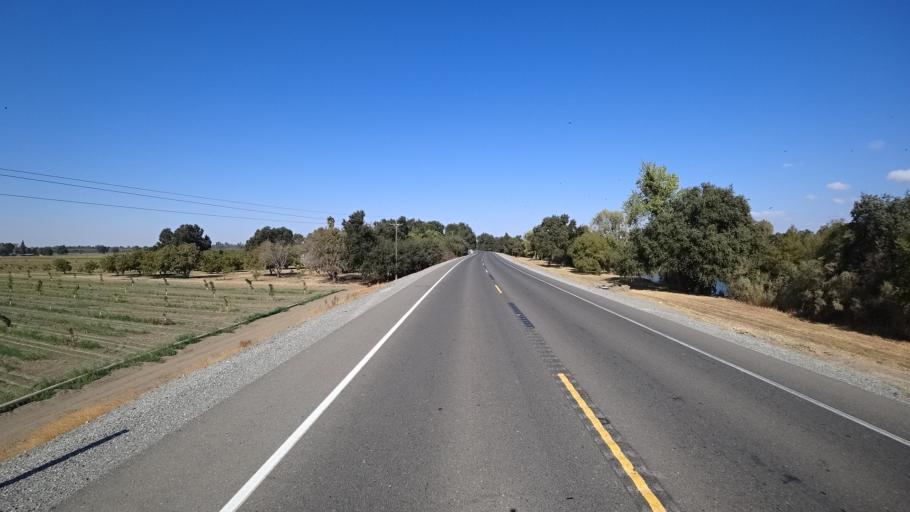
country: US
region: California
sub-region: Yolo County
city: West Sacramento
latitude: 38.6324
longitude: -121.5644
